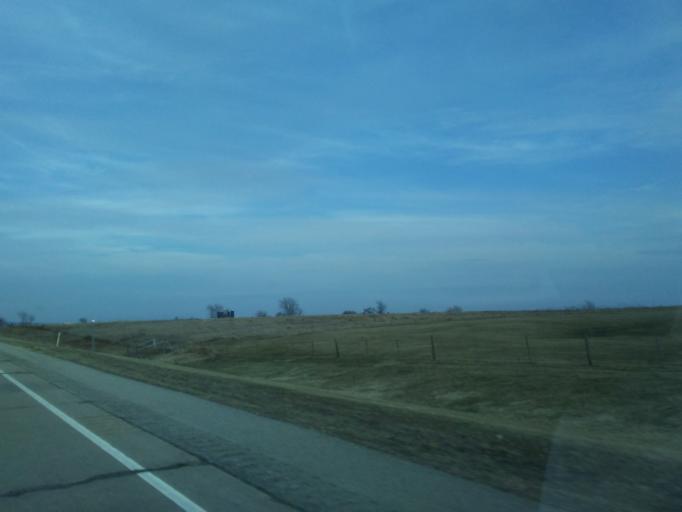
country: US
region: Wisconsin
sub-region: Iowa County
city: Dodgeville
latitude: 42.9728
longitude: -90.0384
